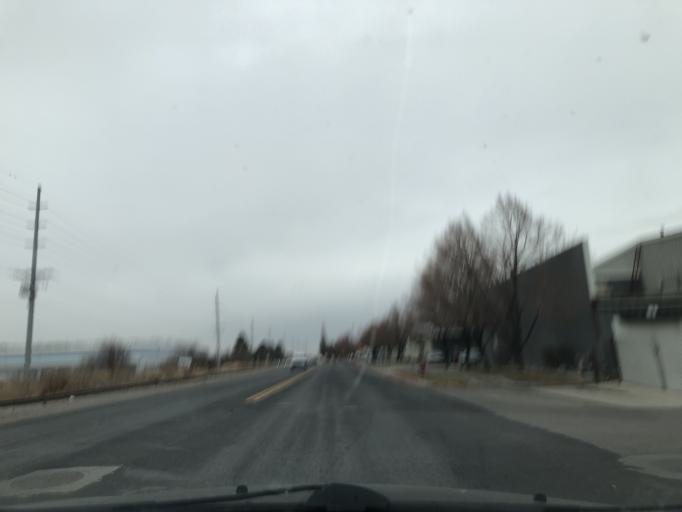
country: US
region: Utah
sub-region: Cache County
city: Logan
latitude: 41.7448
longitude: -111.8493
